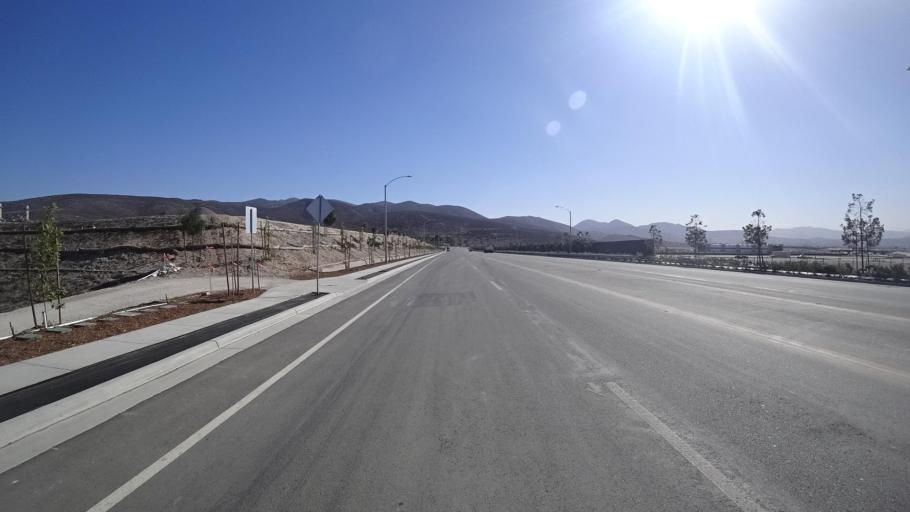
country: MX
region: Baja California
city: Tijuana
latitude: 32.5674
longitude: -116.9179
